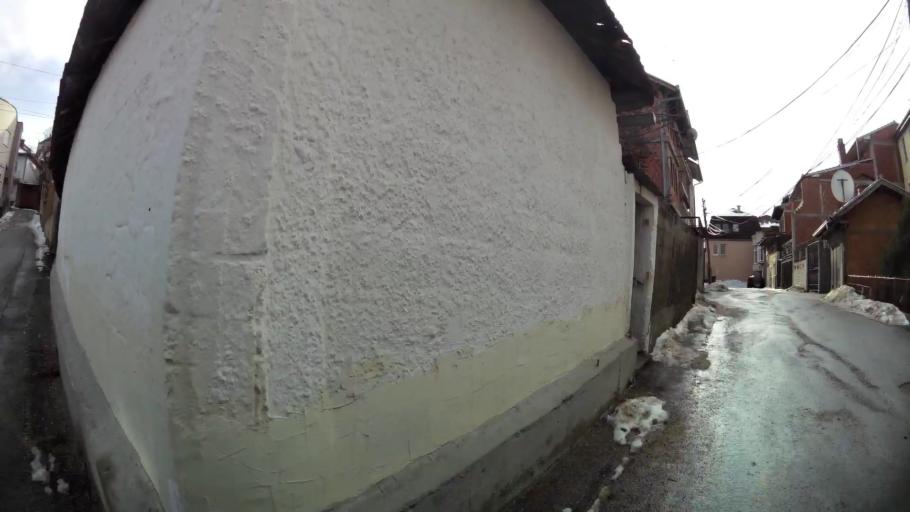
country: XK
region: Pristina
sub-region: Komuna e Prishtines
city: Pristina
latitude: 42.6699
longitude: 21.1746
